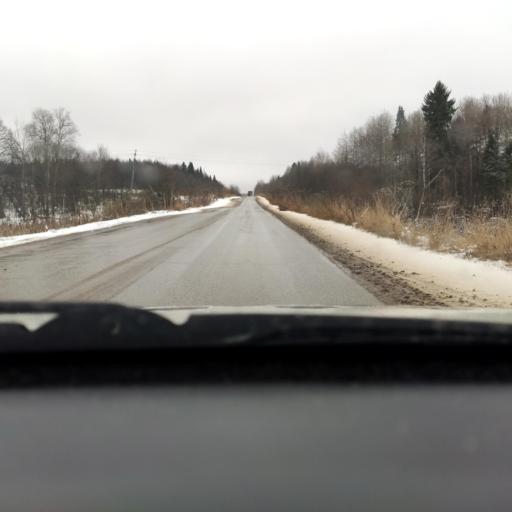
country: RU
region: Perm
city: Ferma
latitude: 57.9900
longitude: 56.3736
